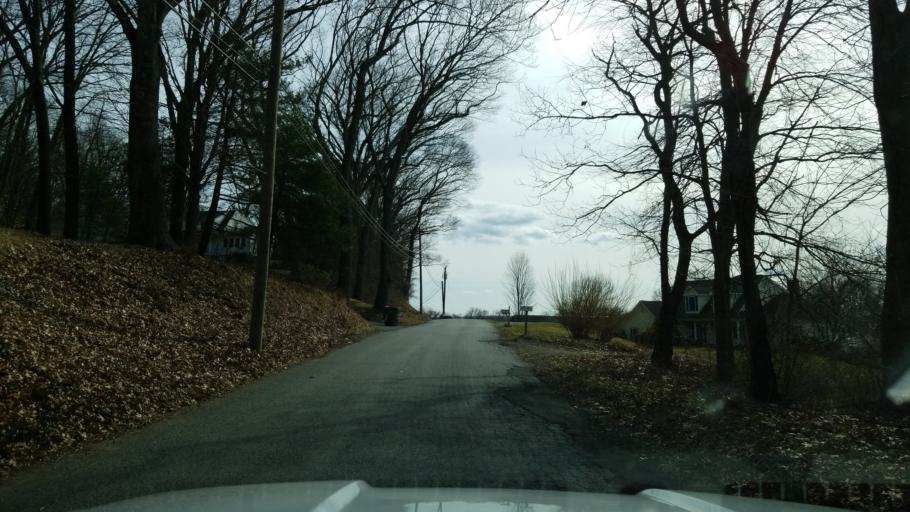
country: US
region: Connecticut
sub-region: Hartford County
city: Glastonbury Center
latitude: 41.6593
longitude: -72.6188
